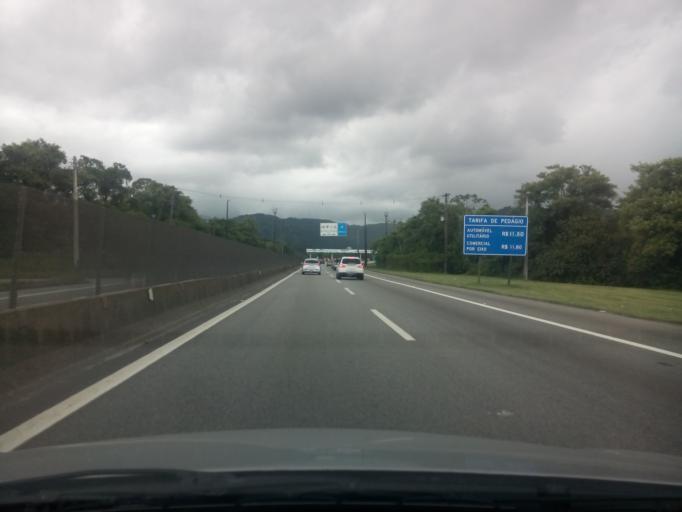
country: BR
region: Sao Paulo
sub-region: Santos
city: Santos
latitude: -23.8982
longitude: -46.3004
